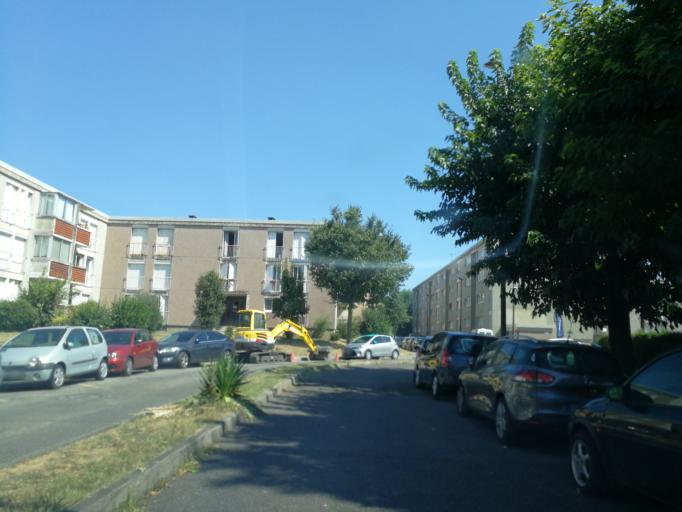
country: FR
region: Midi-Pyrenees
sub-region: Departement de la Haute-Garonne
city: L'Union
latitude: 43.6292
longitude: 1.4691
